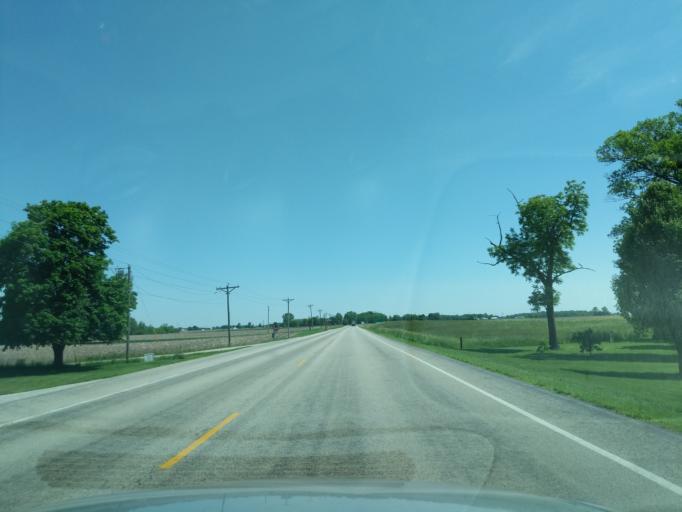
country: US
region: Indiana
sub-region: Huntington County
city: Huntington
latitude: 40.9098
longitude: -85.4787
